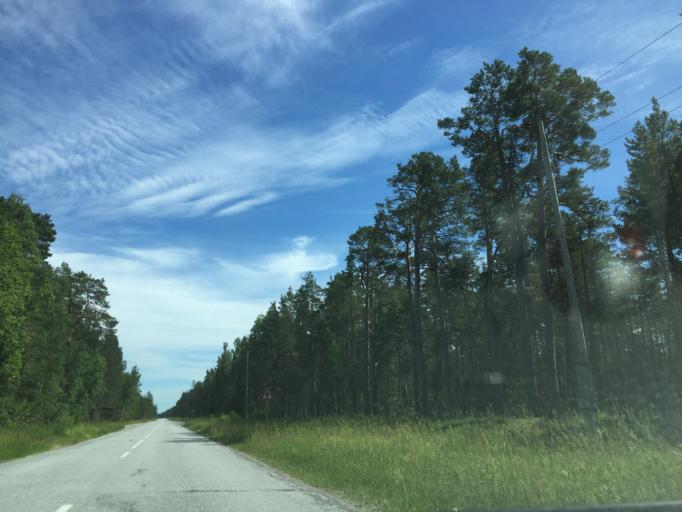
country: LV
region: Rojas
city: Roja
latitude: 57.5671
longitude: 22.6504
